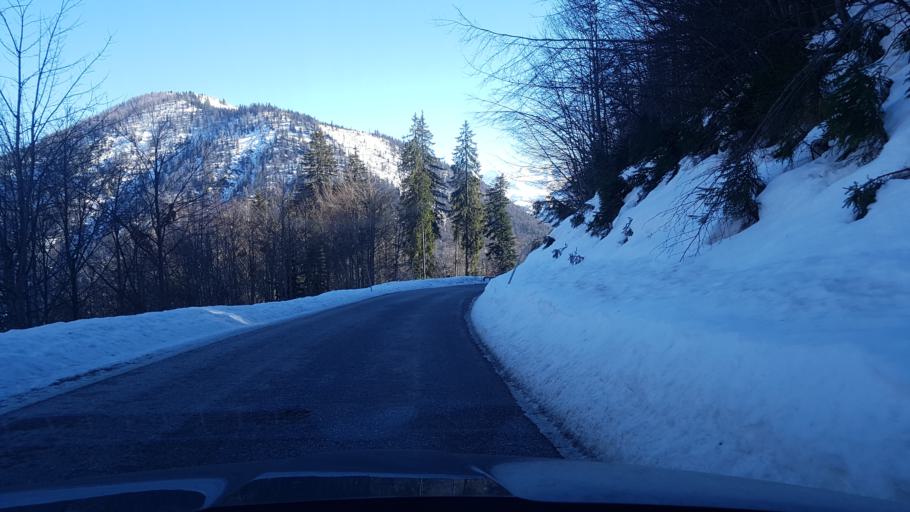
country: AT
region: Salzburg
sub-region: Politischer Bezirk Hallein
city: Abtenau
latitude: 47.6133
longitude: 13.3844
